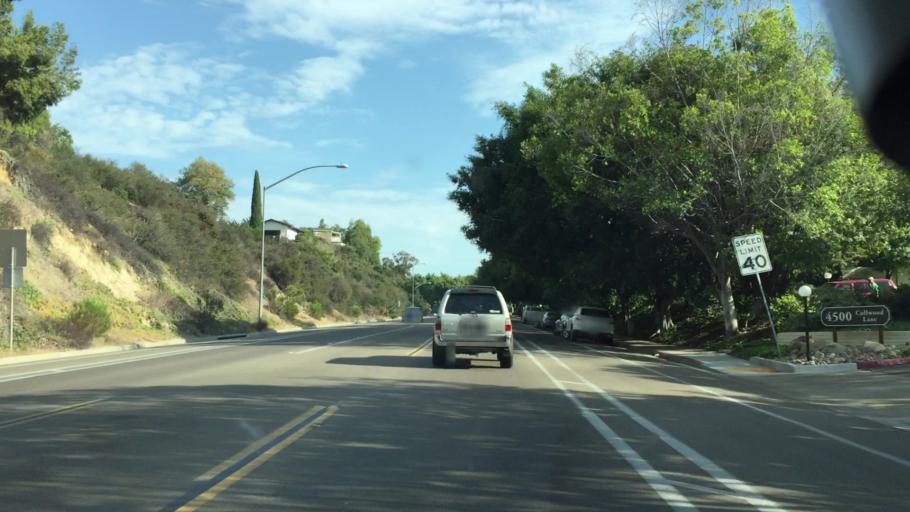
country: US
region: California
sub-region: San Diego County
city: Lemon Grove
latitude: 32.7656
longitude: -117.0836
